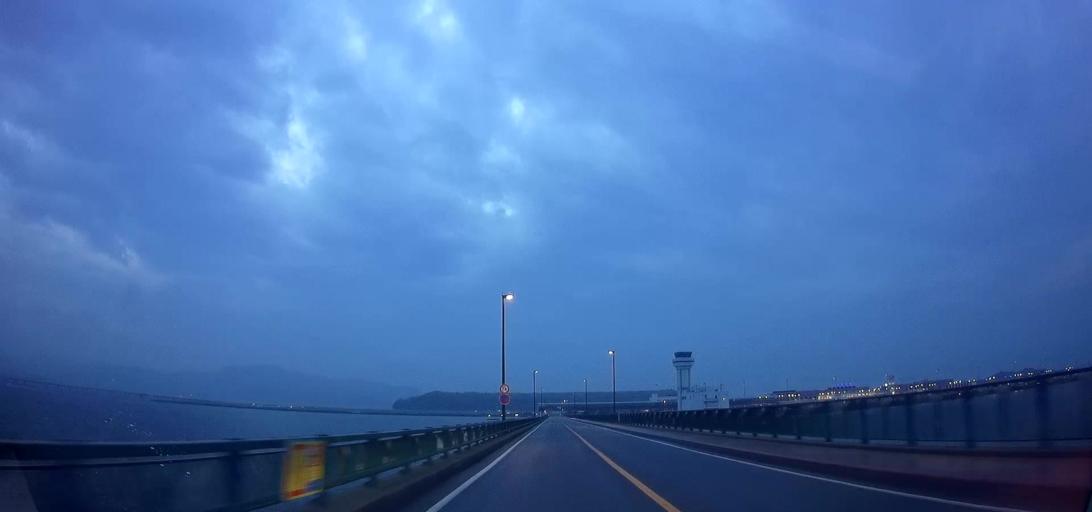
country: JP
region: Nagasaki
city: Omura
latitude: 32.9151
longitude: 129.9297
